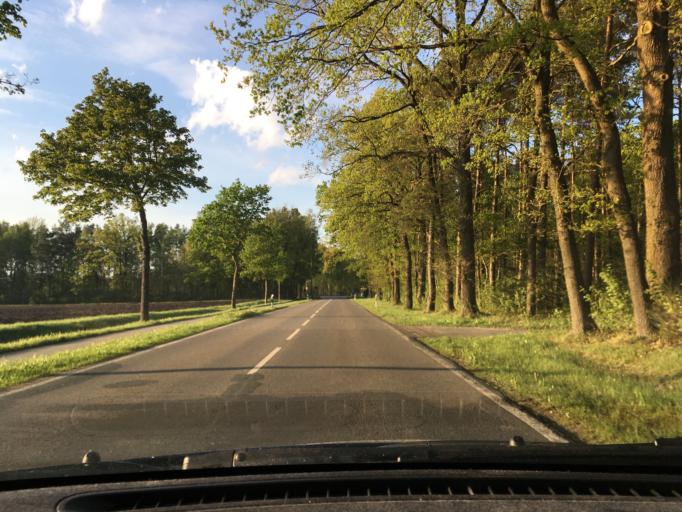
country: DE
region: Lower Saxony
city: Wietzendorf
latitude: 52.9319
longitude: 9.9808
